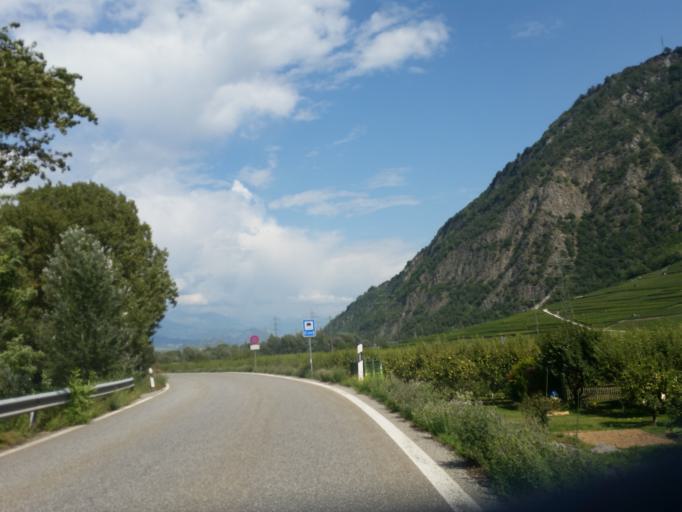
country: CH
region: Valais
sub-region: Martigny District
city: Riddes
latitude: 46.1770
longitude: 7.2309
